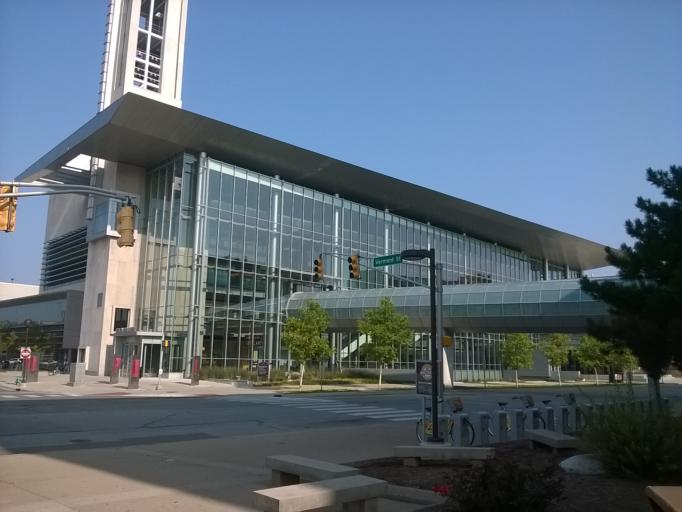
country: US
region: Indiana
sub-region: Marion County
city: Indianapolis
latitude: 39.7733
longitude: -86.1753
